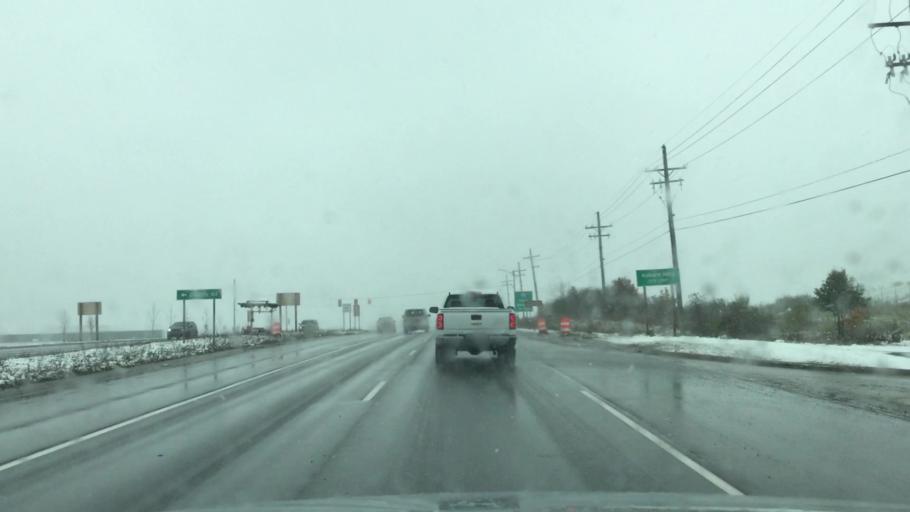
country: US
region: Michigan
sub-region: Oakland County
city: Auburn Hills
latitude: 42.7078
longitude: -83.2429
